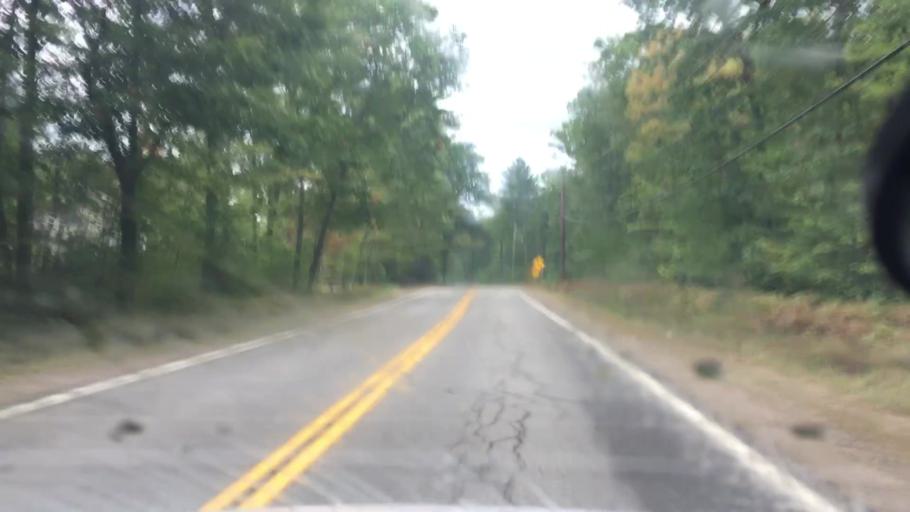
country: US
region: New Hampshire
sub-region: Carroll County
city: Wakefield
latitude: 43.6167
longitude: -70.9971
